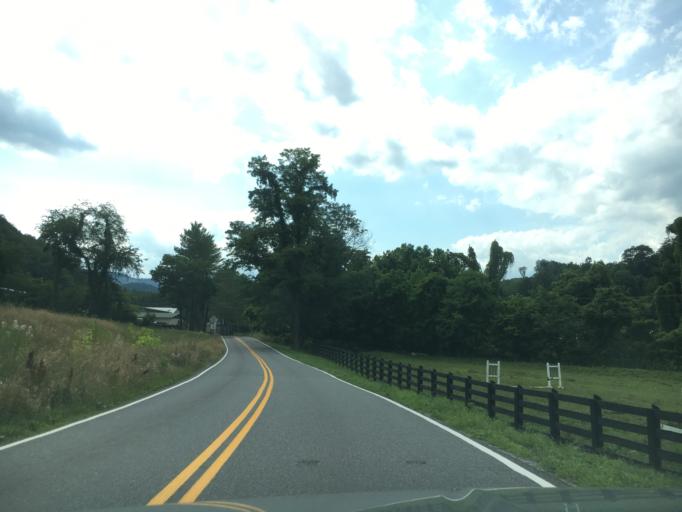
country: US
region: Virginia
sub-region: Roanoke County
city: Narrows
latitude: 37.1393
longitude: -79.9832
